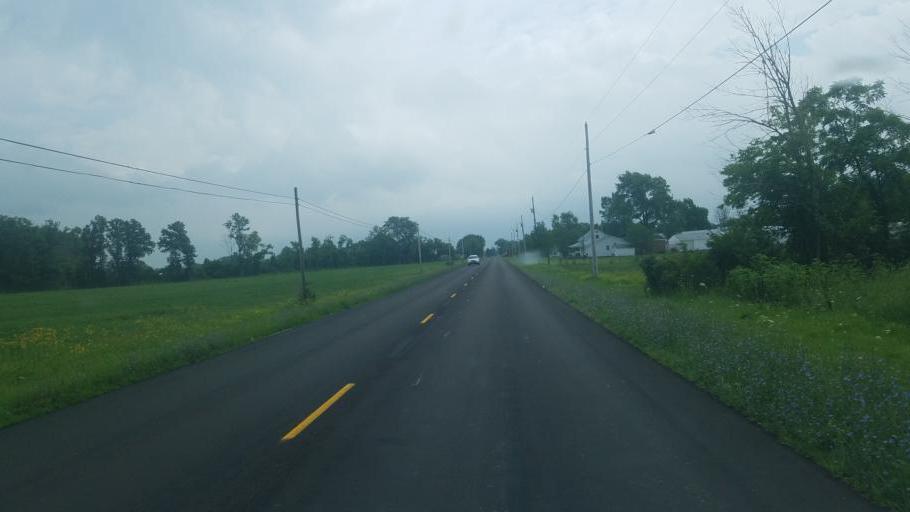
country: US
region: Ohio
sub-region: Logan County
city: Russells Point
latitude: 40.4681
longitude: -83.8374
